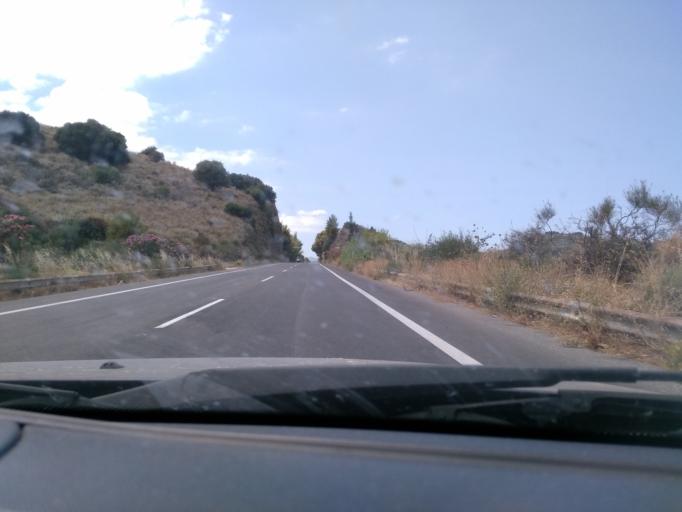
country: GR
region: Crete
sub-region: Nomos Chanias
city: Georgioupolis
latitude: 35.3624
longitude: 24.2440
